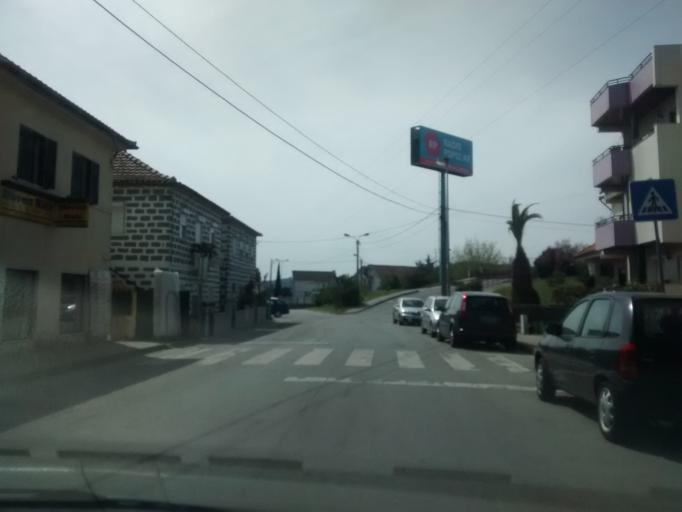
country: PT
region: Braga
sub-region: Braga
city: Braga
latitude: 41.5410
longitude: -8.4401
